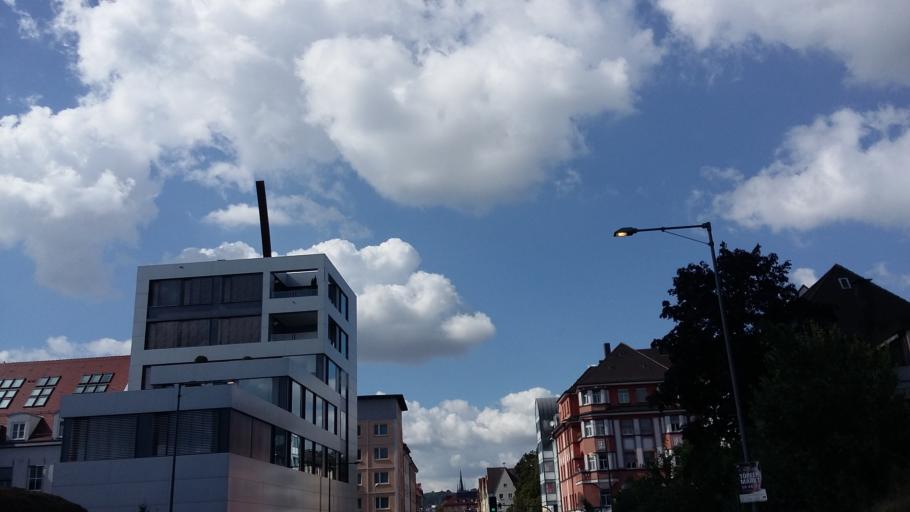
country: DE
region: Bavaria
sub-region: Swabia
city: Neu-Ulm
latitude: 48.3957
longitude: 10.0084
